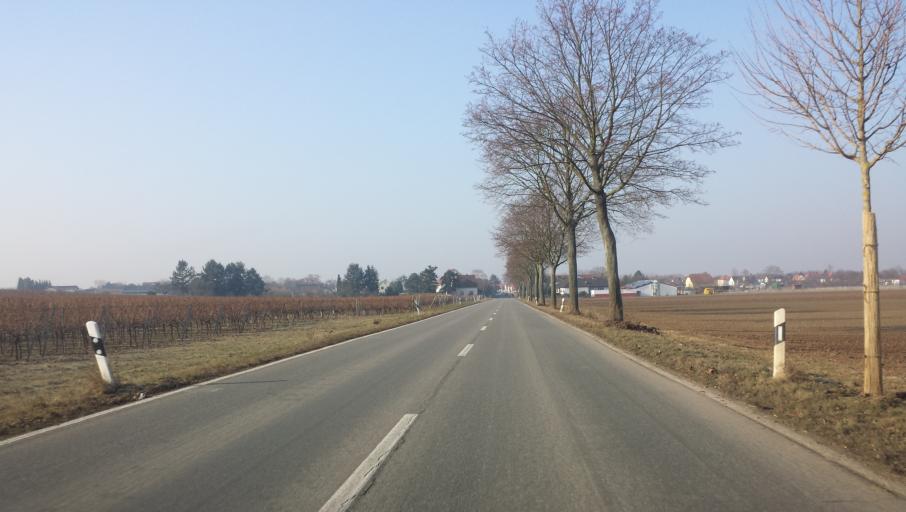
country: DE
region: Rheinland-Pfalz
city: Kleinniedesheim
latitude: 49.6048
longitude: 8.3101
